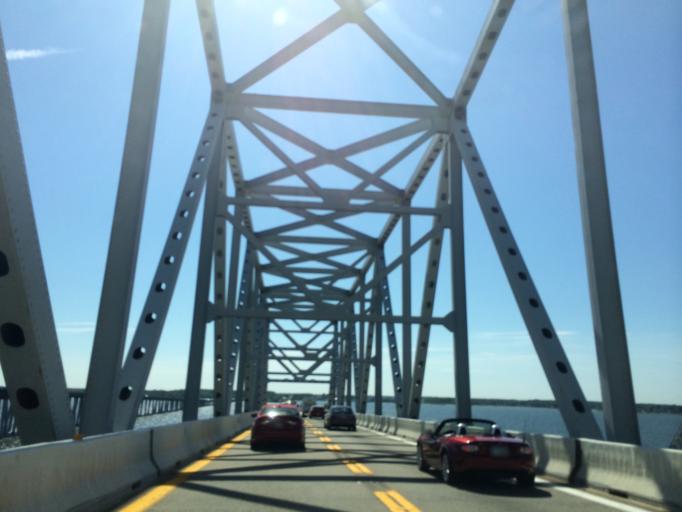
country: US
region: Maryland
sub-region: Queen Anne's County
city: Stevensville
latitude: 38.9874
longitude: -76.3572
